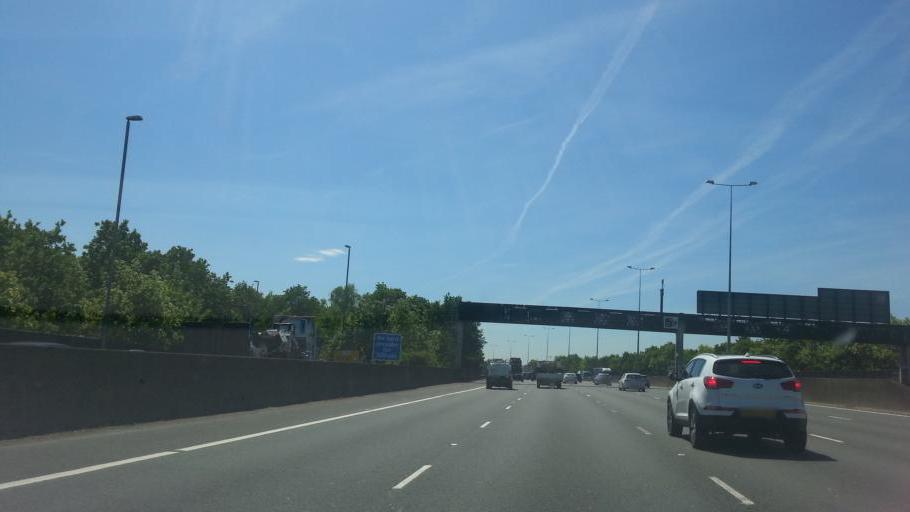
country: GB
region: England
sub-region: Surrey
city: Egham
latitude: 51.4350
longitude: -0.5372
